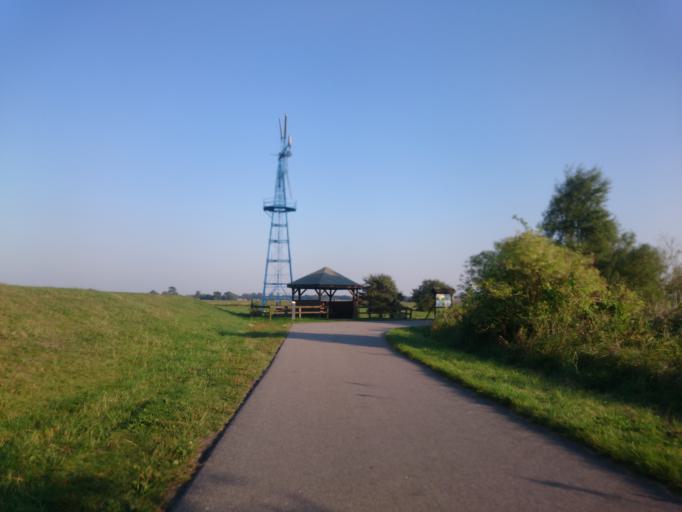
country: DE
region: Mecklenburg-Vorpommern
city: Velgast
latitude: 54.3430
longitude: 12.8095
